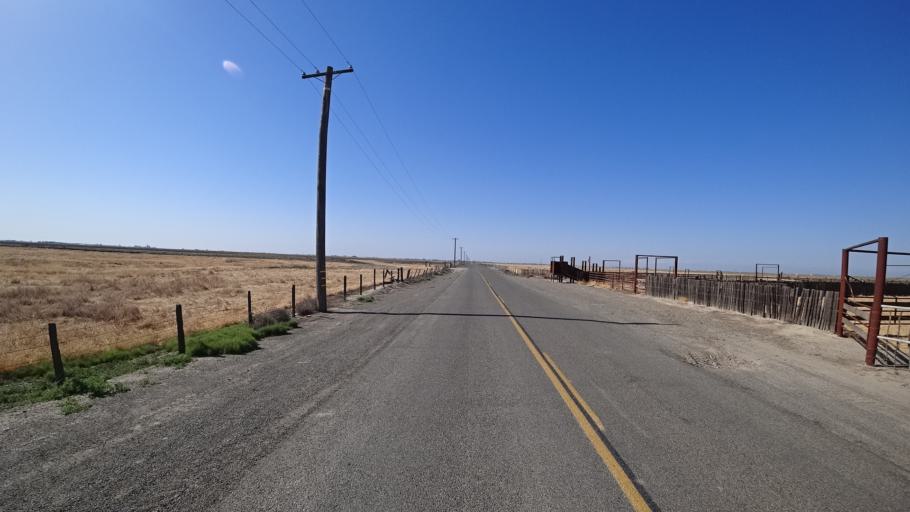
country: US
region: California
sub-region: Kings County
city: Corcoran
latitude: 36.1630
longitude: -119.5649
